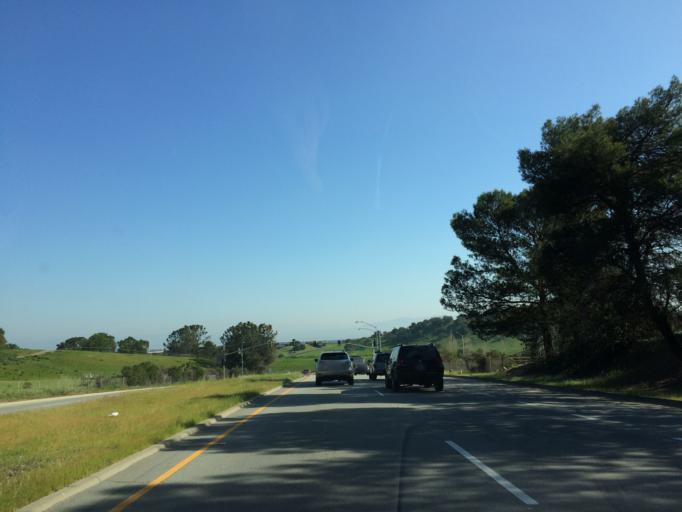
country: US
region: California
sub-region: Santa Clara County
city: Los Altos Hills
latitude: 37.3968
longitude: -122.1592
